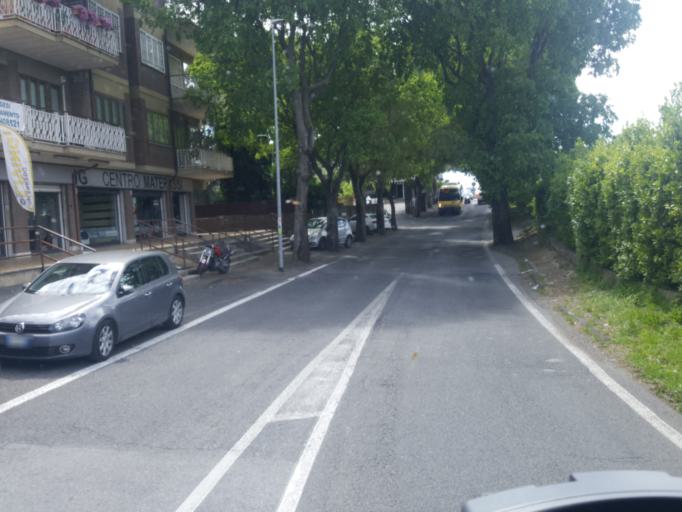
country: IT
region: Latium
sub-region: Citta metropolitana di Roma Capitale
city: La Massimina-Casal Lumbroso
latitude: 41.8838
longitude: 12.3612
